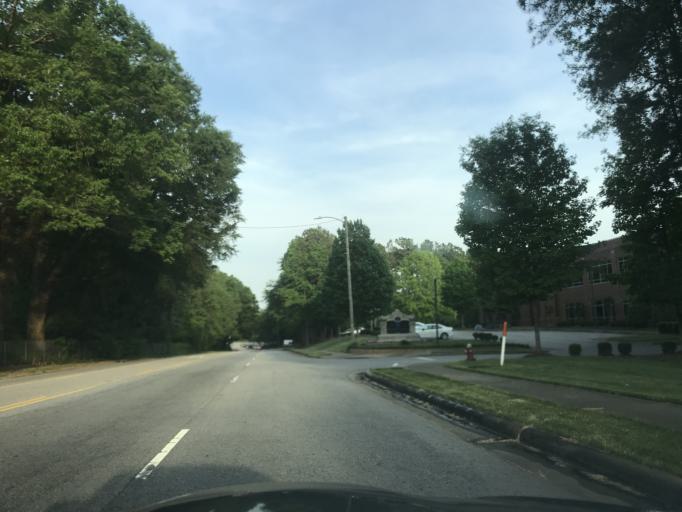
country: US
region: North Carolina
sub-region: Wake County
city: Raleigh
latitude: 35.7434
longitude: -78.6448
